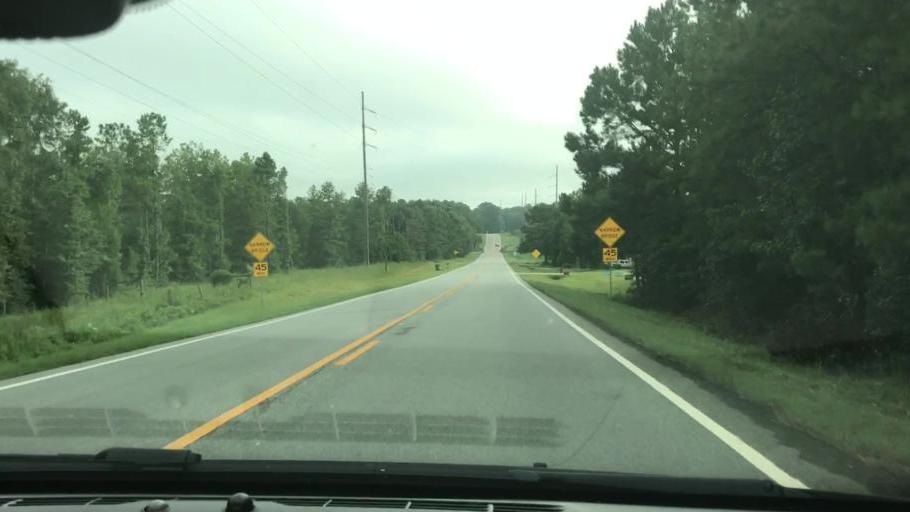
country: US
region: Georgia
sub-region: Quitman County
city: Georgetown
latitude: 31.8435
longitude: -85.0768
